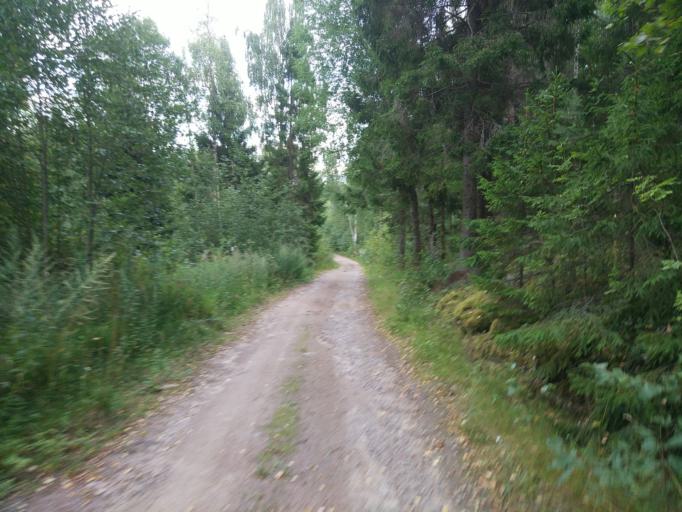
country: RU
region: Leningrad
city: Kuznechnoye
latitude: 61.1090
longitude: 29.6148
